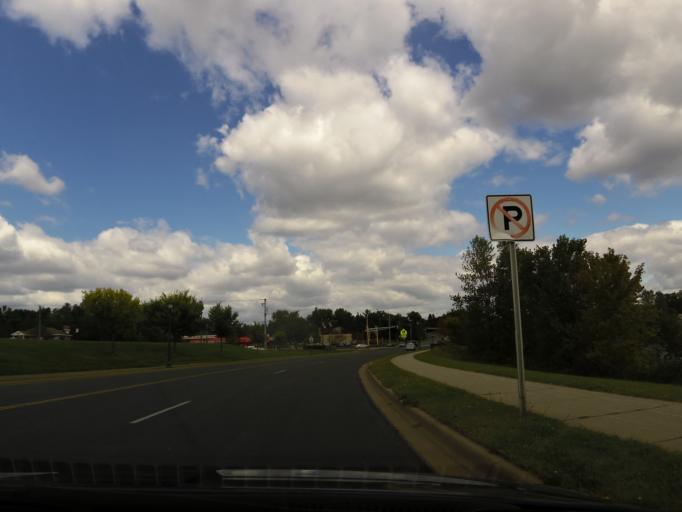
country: US
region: Minnesota
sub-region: Dakota County
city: Inver Grove Heights
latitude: 44.8325
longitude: -93.0440
